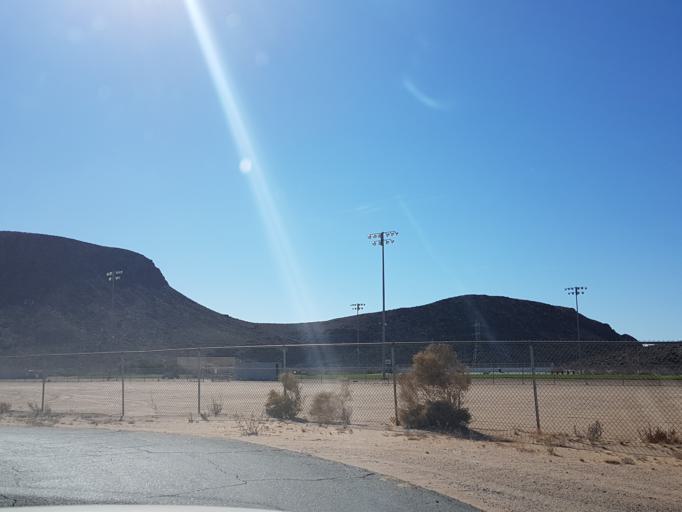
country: US
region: California
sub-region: San Bernardino County
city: Barstow
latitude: 34.8983
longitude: -116.8892
